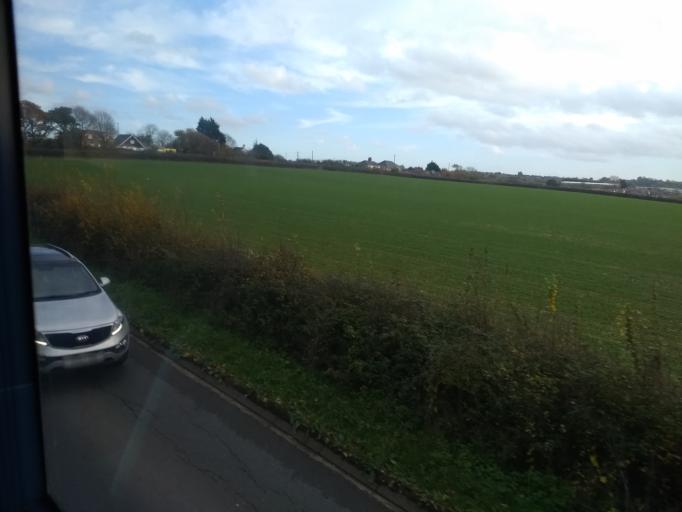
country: GB
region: England
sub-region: Isle of Wight
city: Newport
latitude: 50.7051
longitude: -1.3265
